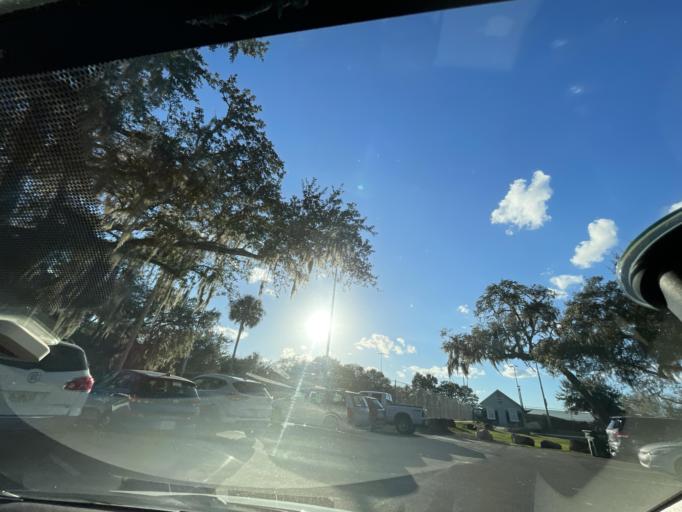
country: US
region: Florida
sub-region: Volusia County
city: Ormond Beach
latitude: 29.2865
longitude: -81.0860
